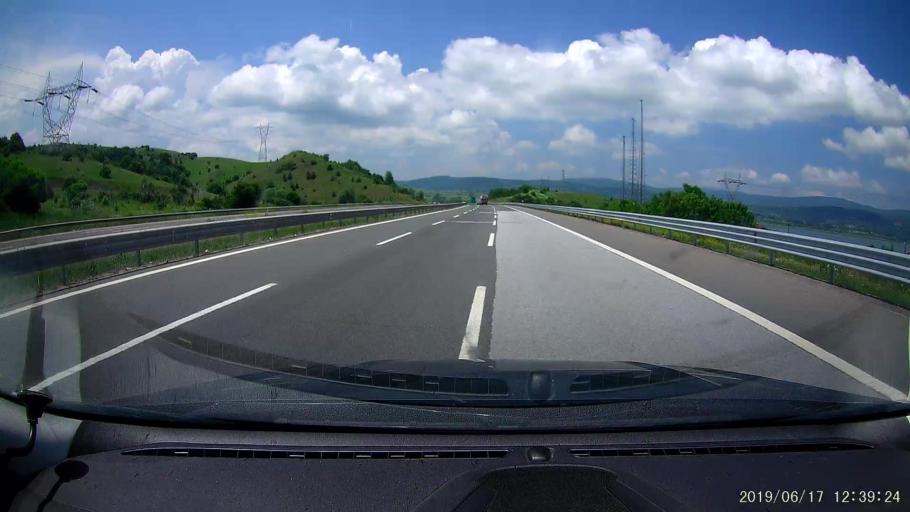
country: TR
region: Bolu
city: Yenicaga
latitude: 40.7656
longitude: 32.0371
